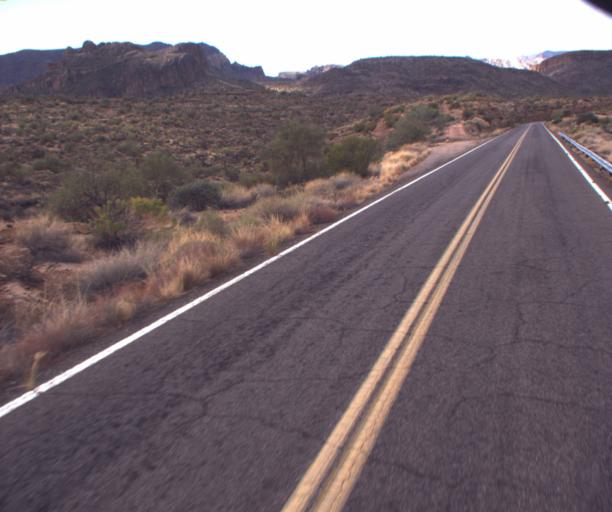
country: US
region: Arizona
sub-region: Pinal County
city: Apache Junction
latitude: 33.5331
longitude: -111.3560
